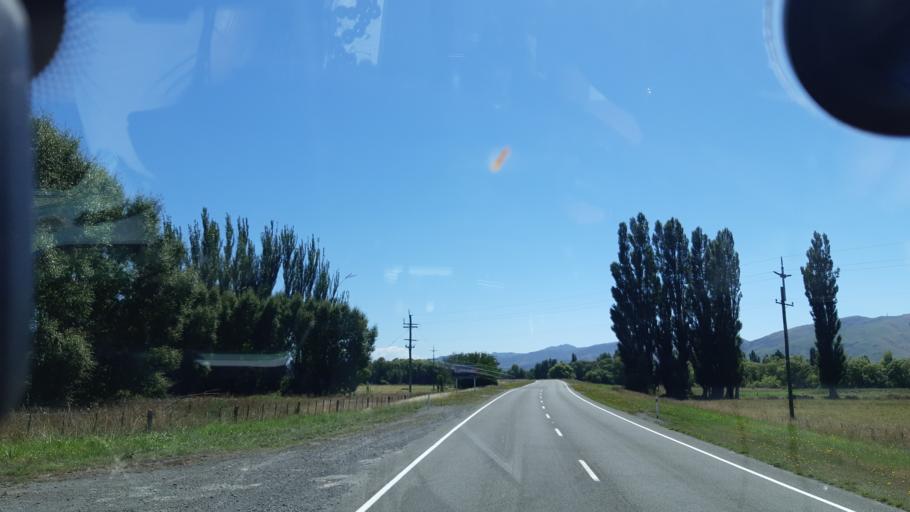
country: NZ
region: Canterbury
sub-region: Kaikoura District
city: Kaikoura
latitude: -42.7286
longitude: 173.2771
